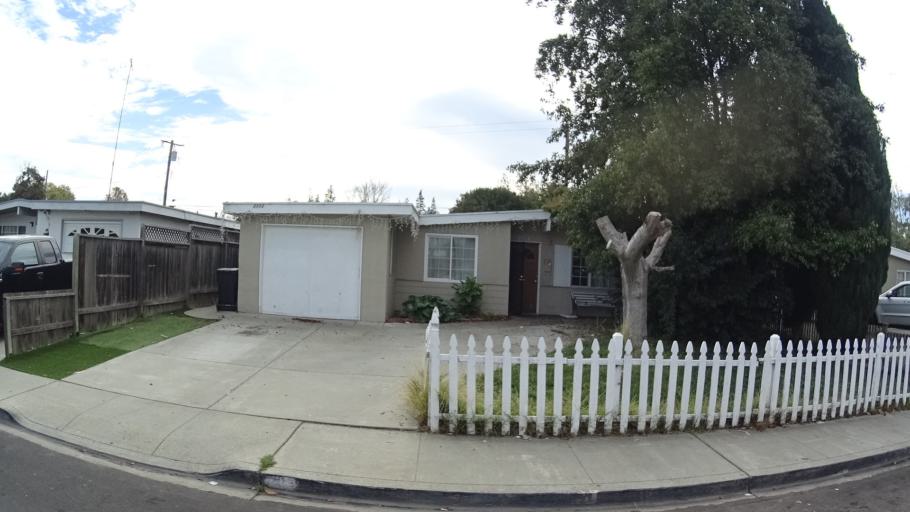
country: US
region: California
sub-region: Santa Clara County
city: Santa Clara
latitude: 37.3608
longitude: -121.9548
